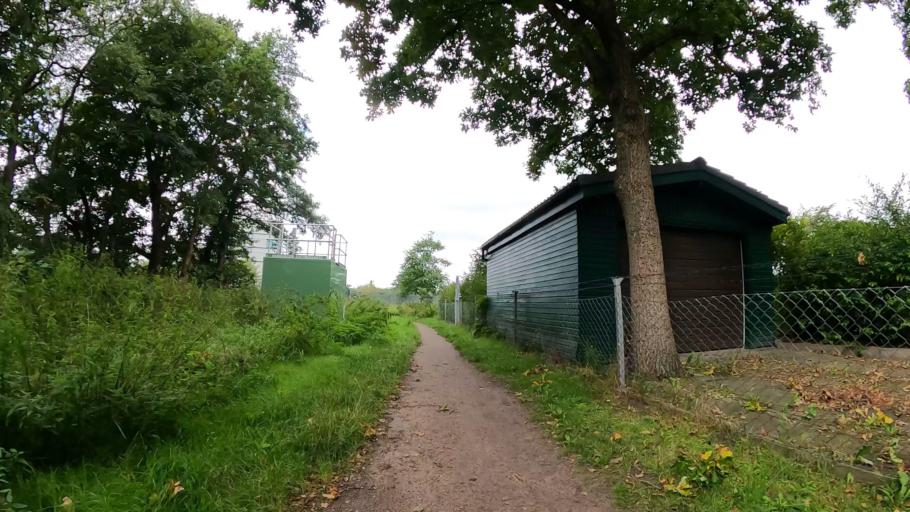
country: DE
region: Lower Saxony
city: Neu Wulmstorf
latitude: 53.4809
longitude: 9.8577
